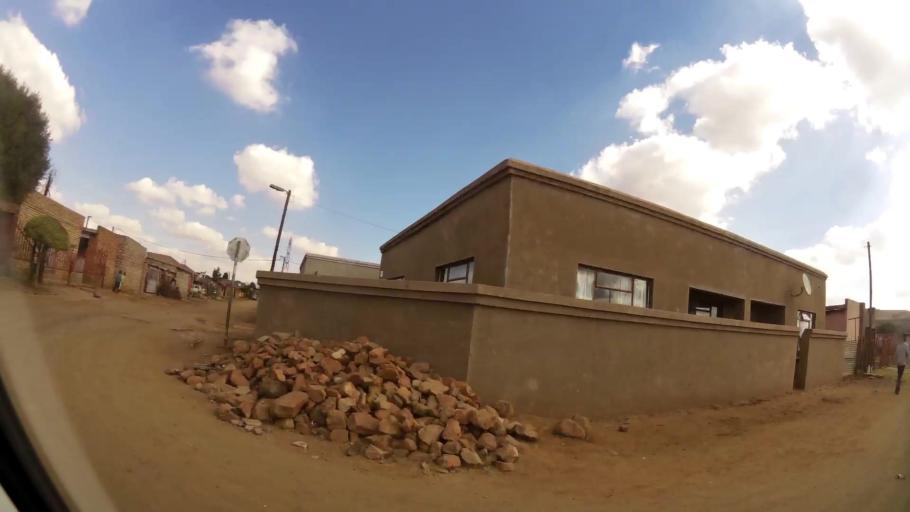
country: ZA
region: Gauteng
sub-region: City of Tshwane Metropolitan Municipality
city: Cullinan
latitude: -25.7063
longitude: 28.3977
